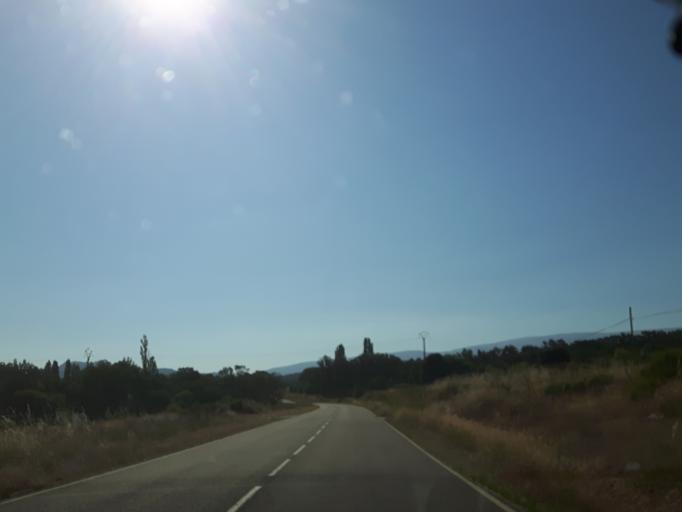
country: ES
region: Castille and Leon
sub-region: Provincia de Salamanca
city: Valdehijaderos
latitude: 40.4217
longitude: -5.8668
